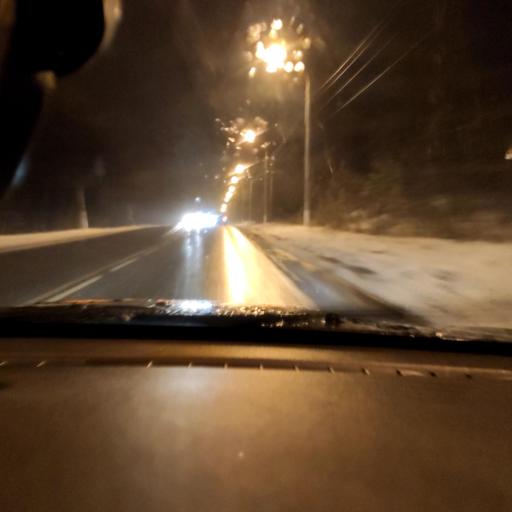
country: RU
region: Samara
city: Tol'yatti
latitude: 53.4735
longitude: 49.4005
